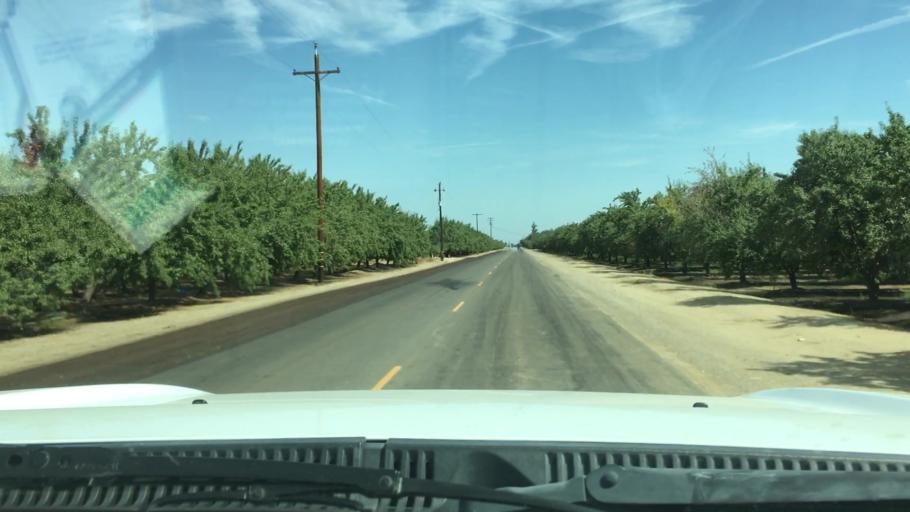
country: US
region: California
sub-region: Kern County
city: Shafter
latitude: 35.5040
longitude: -119.3501
